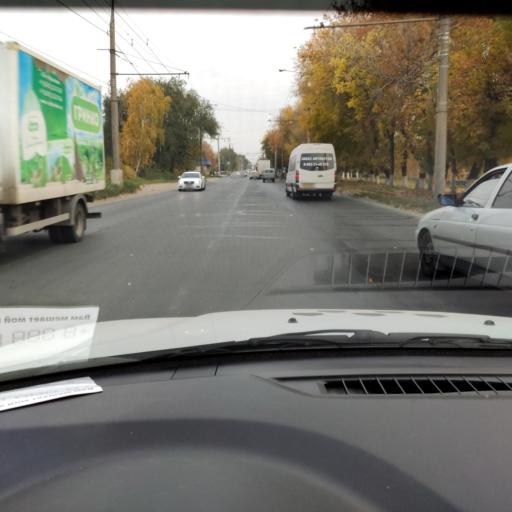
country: RU
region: Samara
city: Tol'yatti
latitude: 53.5388
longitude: 49.4424
